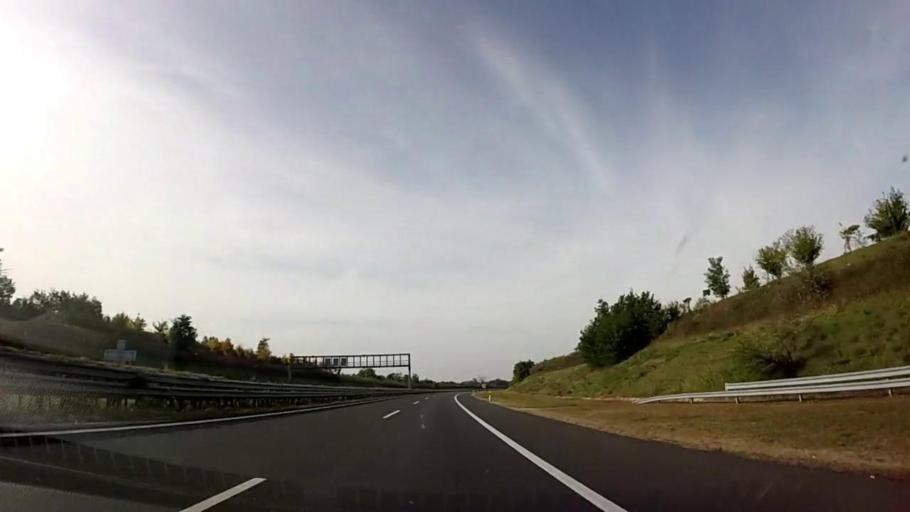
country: HU
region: Somogy
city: Balatonszarszo
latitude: 46.8126
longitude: 17.8461
